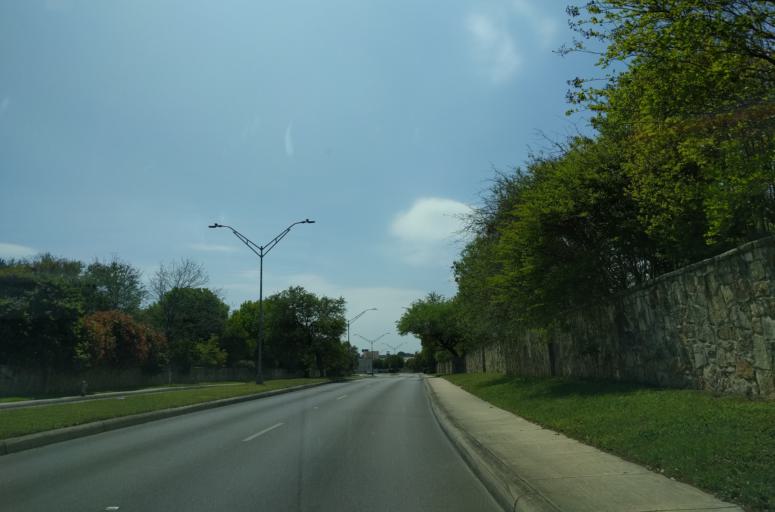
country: US
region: Texas
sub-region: Bexar County
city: Shavano Park
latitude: 29.5689
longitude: -98.5858
